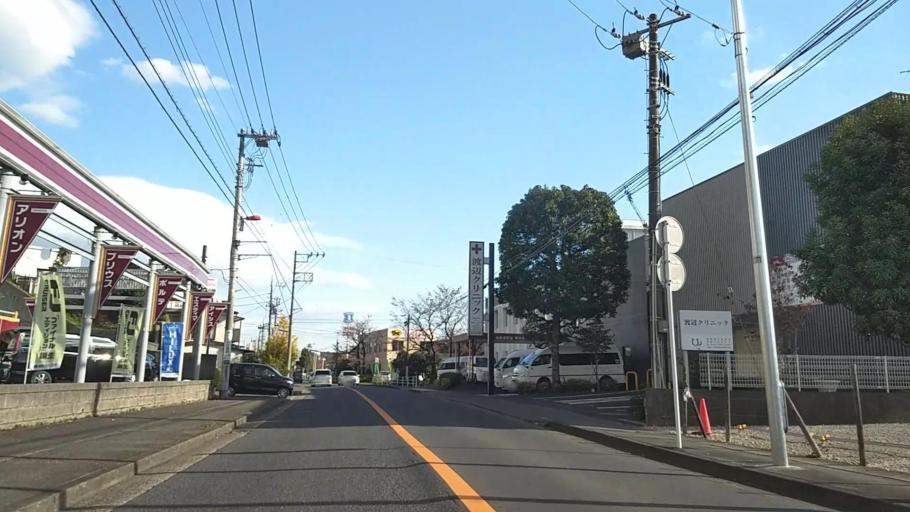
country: JP
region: Tokyo
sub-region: Machida-shi
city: Machida
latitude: 35.5787
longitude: 139.5026
